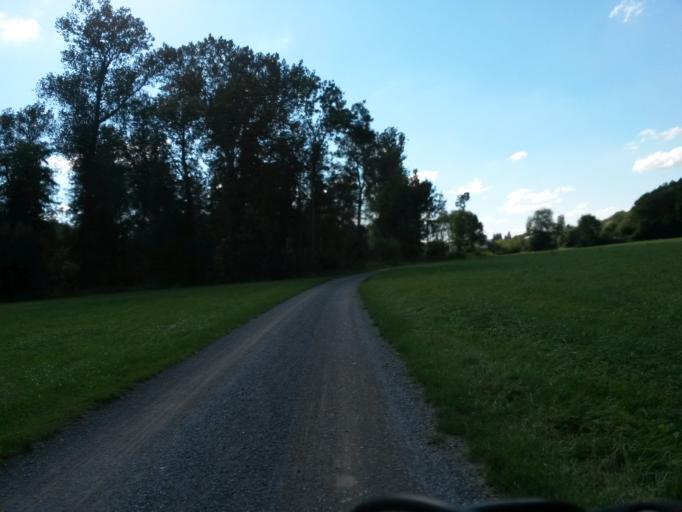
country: DE
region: Baden-Wuerttemberg
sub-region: Regierungsbezirk Stuttgart
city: Oberriexingen
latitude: 48.9337
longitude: 9.0399
